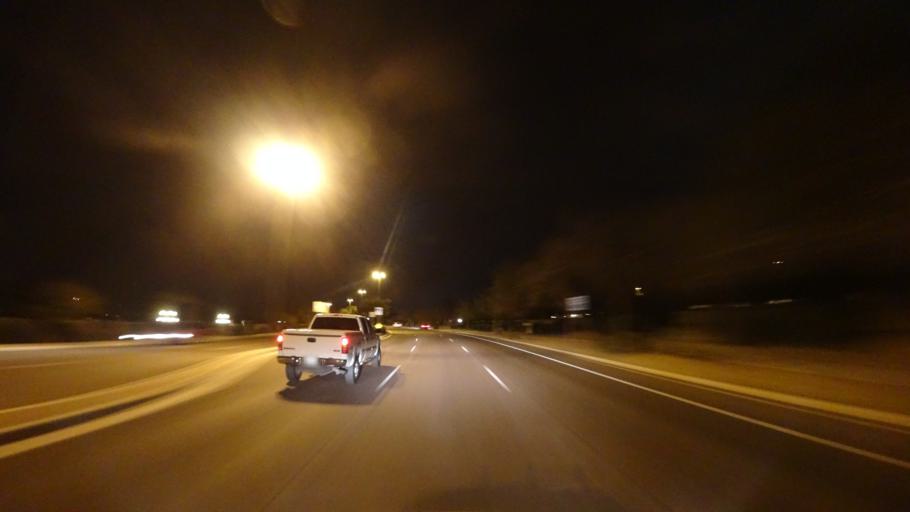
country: US
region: Arizona
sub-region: Maricopa County
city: Gilbert
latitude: 33.3138
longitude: -111.7576
